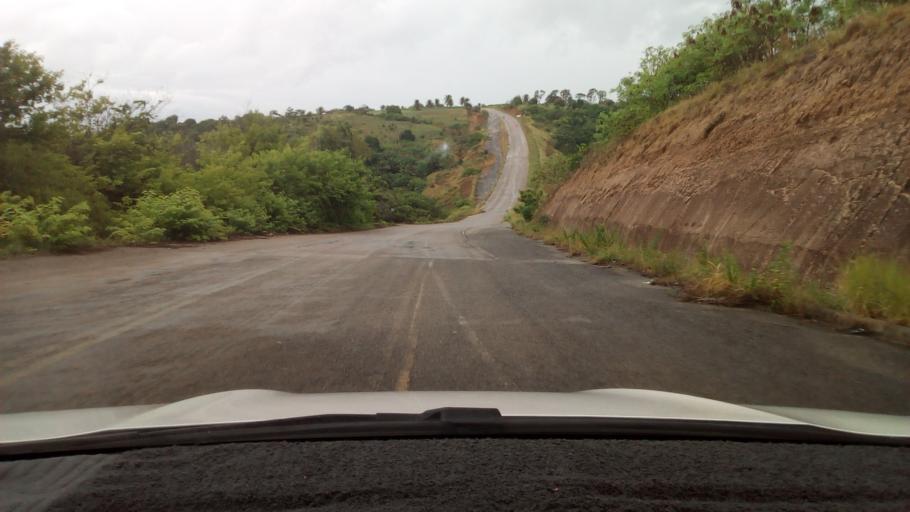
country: BR
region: Paraiba
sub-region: Pitimbu
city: Pitimbu
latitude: -7.4176
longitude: -34.8279
